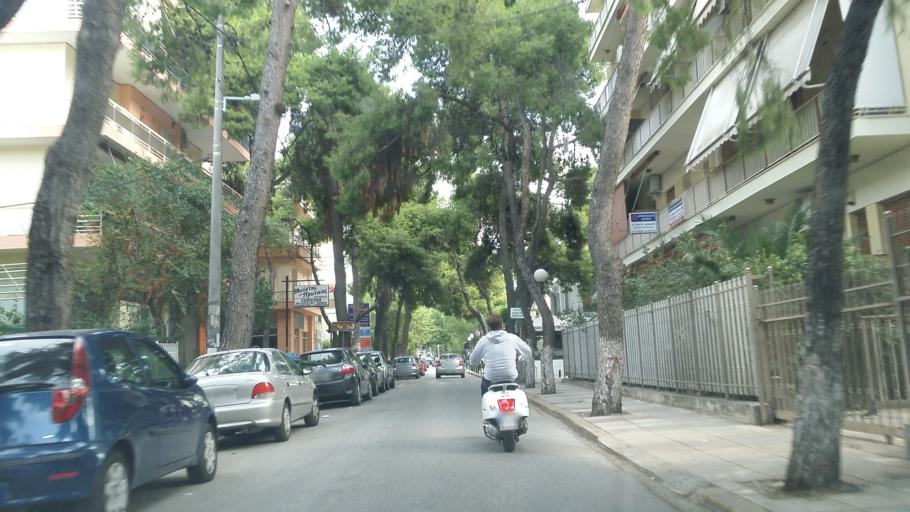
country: GR
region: Attica
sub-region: Nomarchia Athinas
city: Irakleio
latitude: 38.0483
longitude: 23.7658
